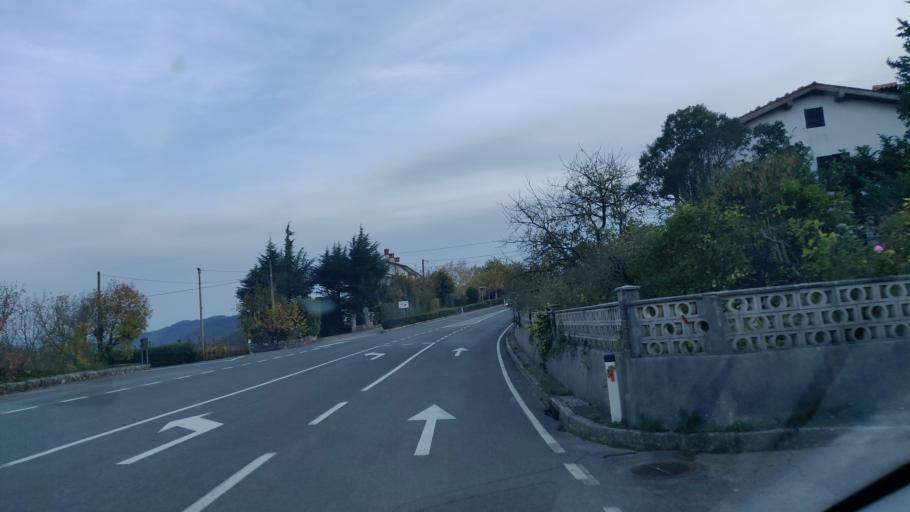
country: SI
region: Ajdovscina
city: Lokavec
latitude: 45.8154
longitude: 13.8496
